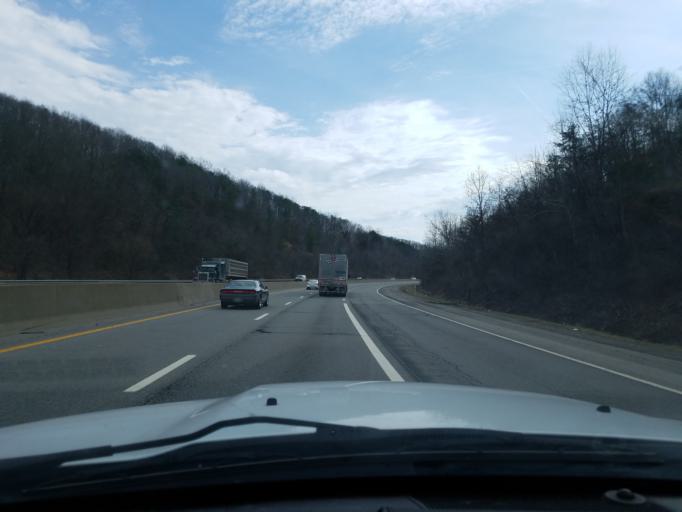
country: US
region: West Virginia
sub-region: Kanawha County
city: Nitro
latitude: 38.4390
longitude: -81.8296
